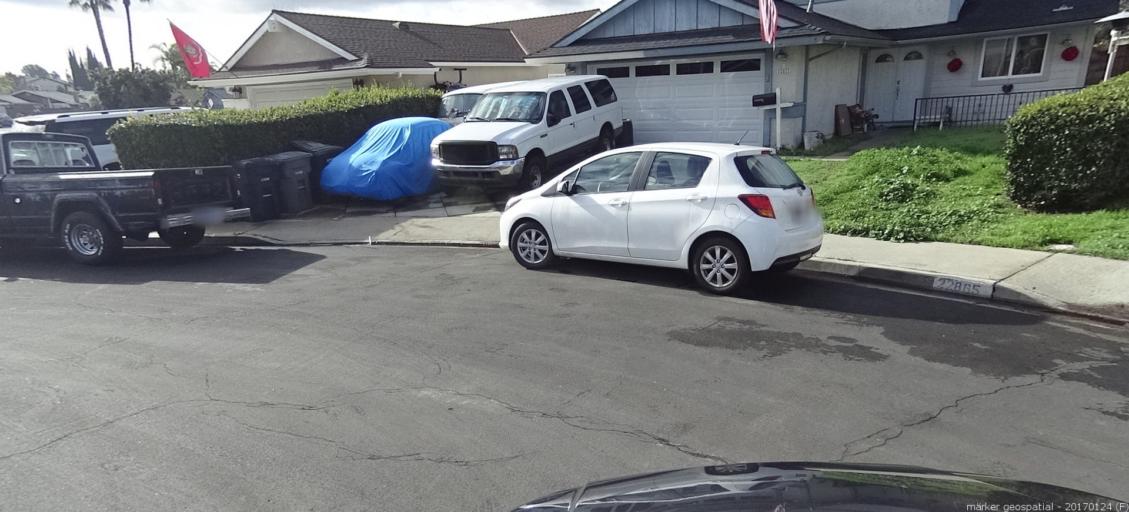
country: US
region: California
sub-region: Orange County
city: Laguna Hills
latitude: 33.6304
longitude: -117.7143
